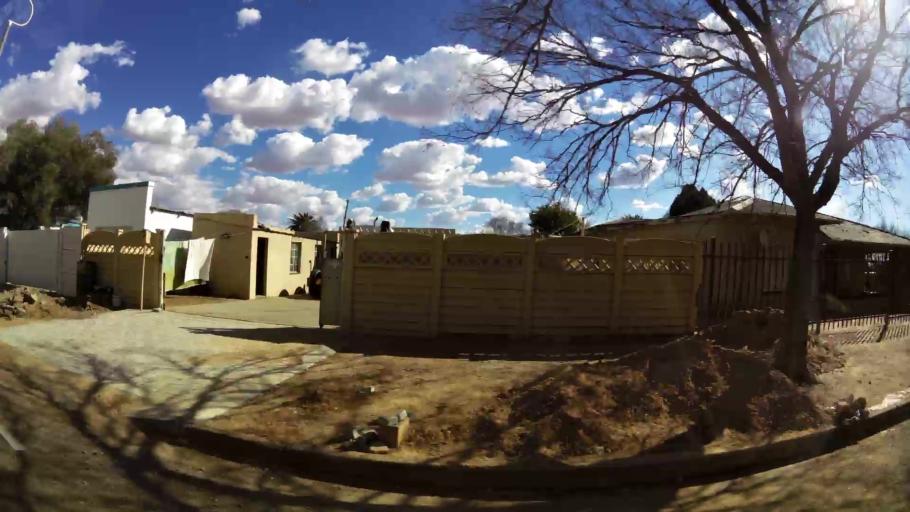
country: ZA
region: North-West
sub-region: Dr Kenneth Kaunda District Municipality
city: Klerksdorp
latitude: -26.8587
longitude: 26.6490
